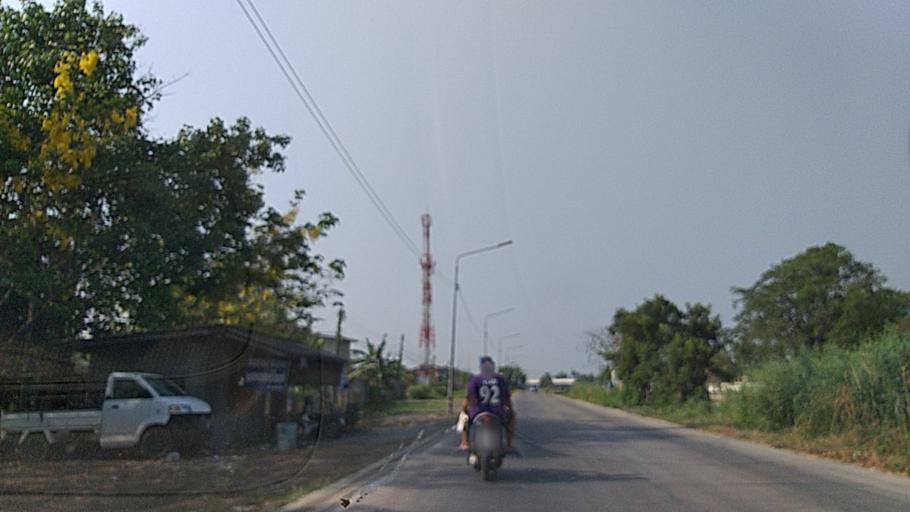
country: TH
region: Pathum Thani
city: Thanyaburi
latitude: 14.0076
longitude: 100.7098
